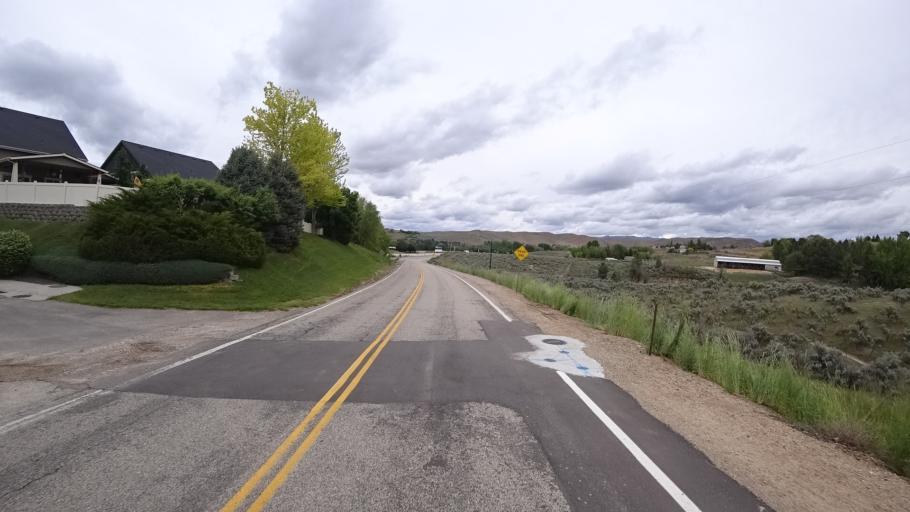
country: US
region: Idaho
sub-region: Ada County
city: Eagle
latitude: 43.7161
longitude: -116.3177
